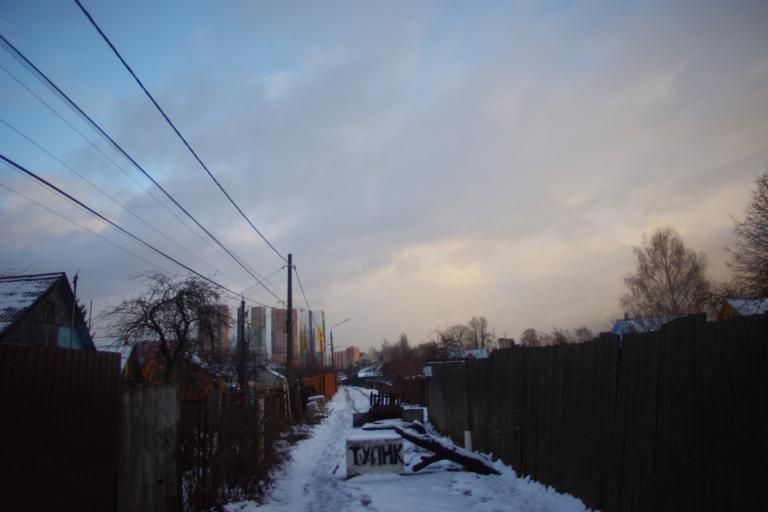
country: RU
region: Moskovskaya
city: Pavshino
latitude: 55.8096
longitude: 37.3468
